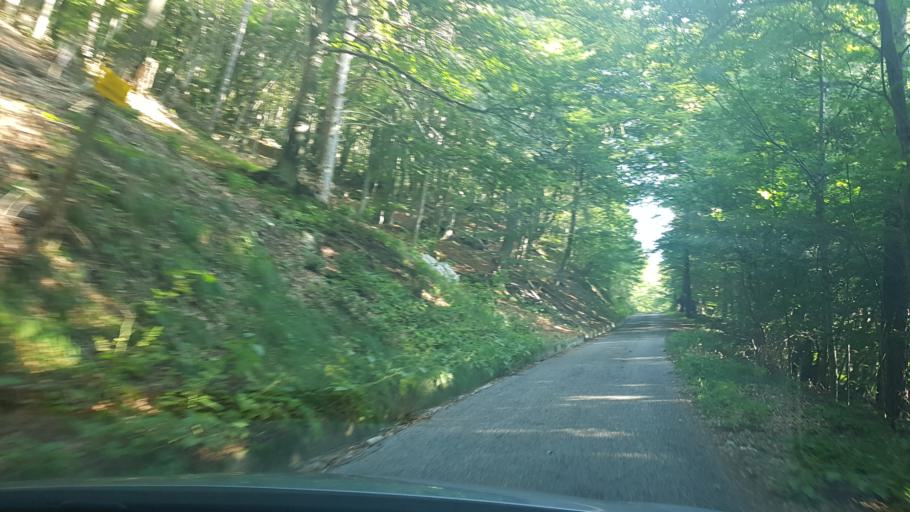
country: IT
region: Friuli Venezia Giulia
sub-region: Provincia di Udine
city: Moggio Udinese
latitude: 46.4419
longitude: 13.2118
